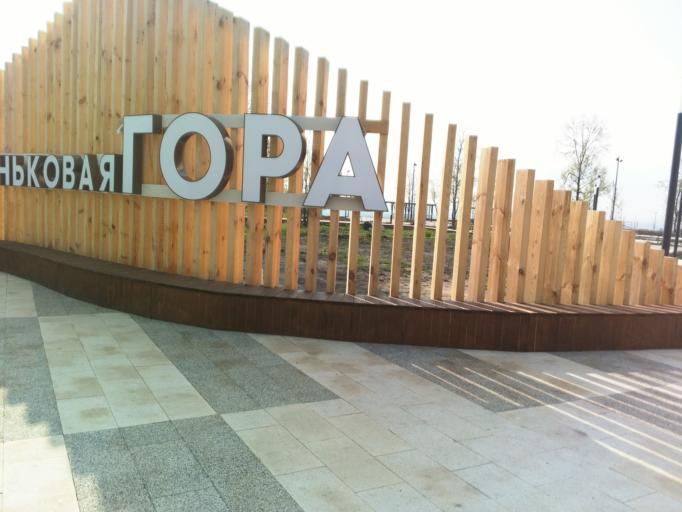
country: RU
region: Voronezj
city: Kalach
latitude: 50.4150
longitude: 41.0018
